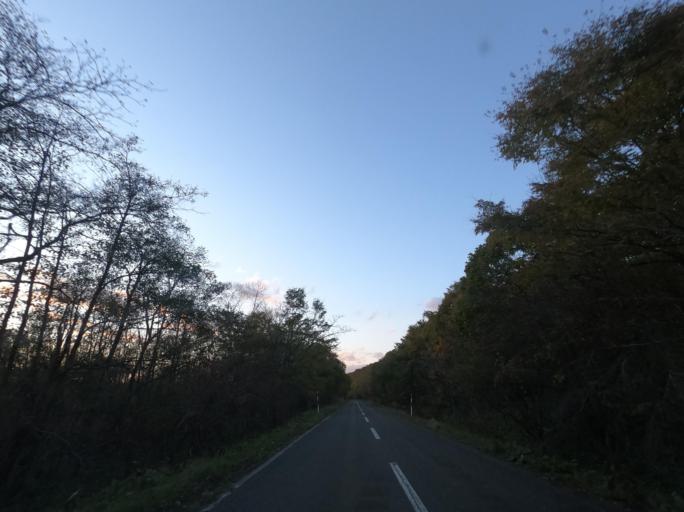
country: JP
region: Hokkaido
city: Kushiro
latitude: 43.2157
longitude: 144.4521
